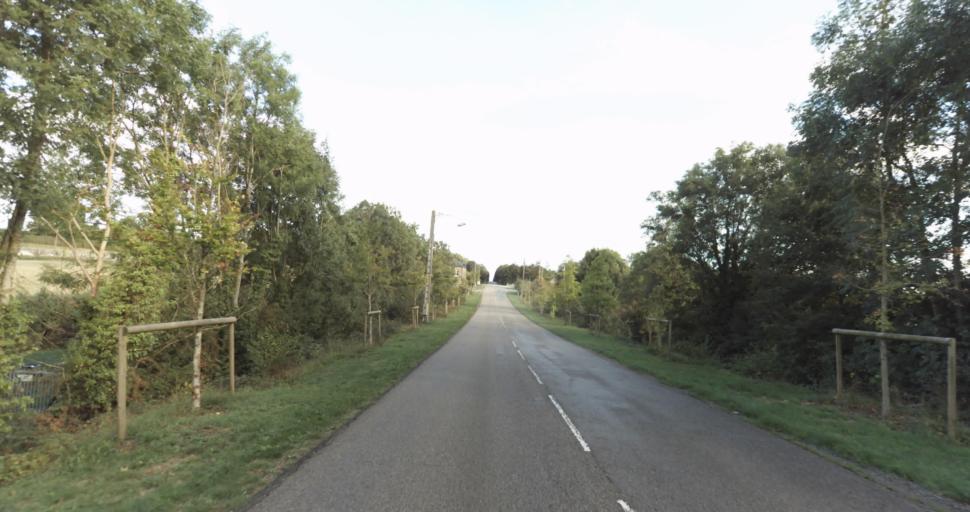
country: FR
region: Lower Normandy
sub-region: Departement de l'Orne
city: Sainte-Gauburge-Sainte-Colombe
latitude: 48.7387
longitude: 0.3923
